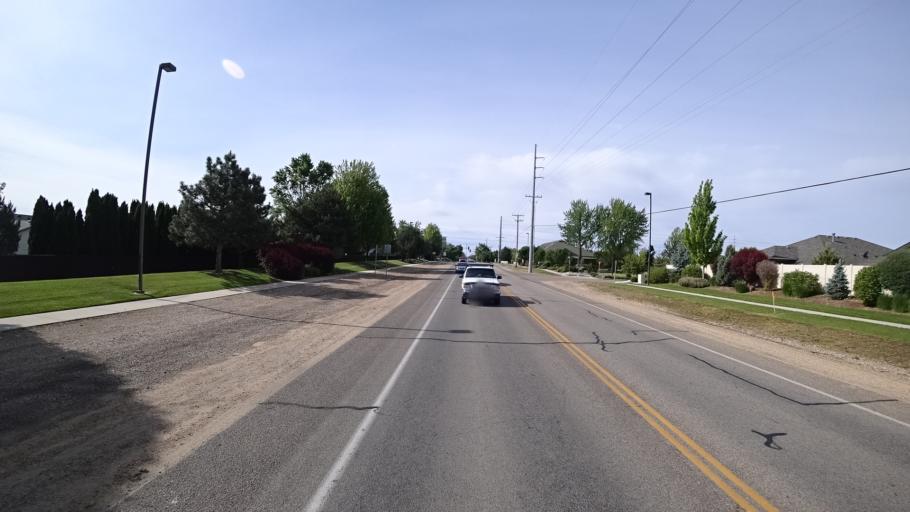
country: US
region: Idaho
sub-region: Ada County
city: Meridian
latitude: 43.5627
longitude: -116.3344
